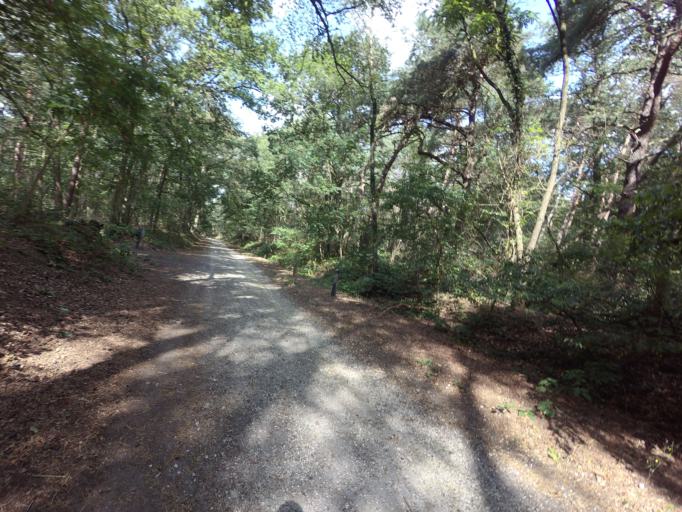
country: NL
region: Limburg
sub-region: Gemeente Heerlen
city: Heerlen
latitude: 50.9093
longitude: 6.0088
